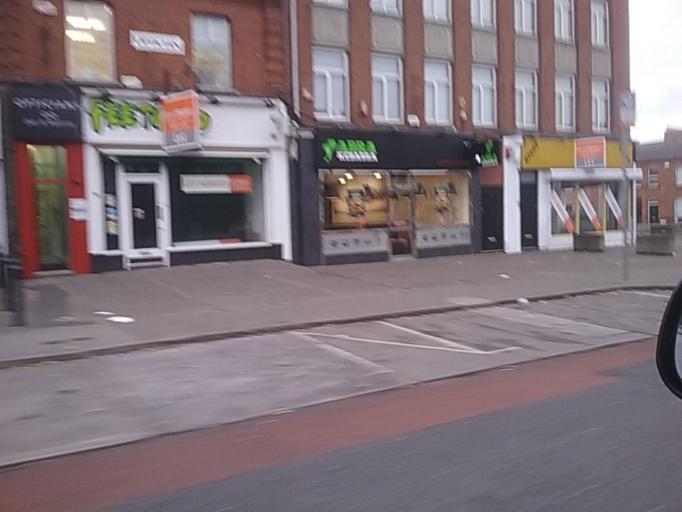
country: IE
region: Leinster
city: Drumcondra
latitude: 53.3691
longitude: -6.2546
